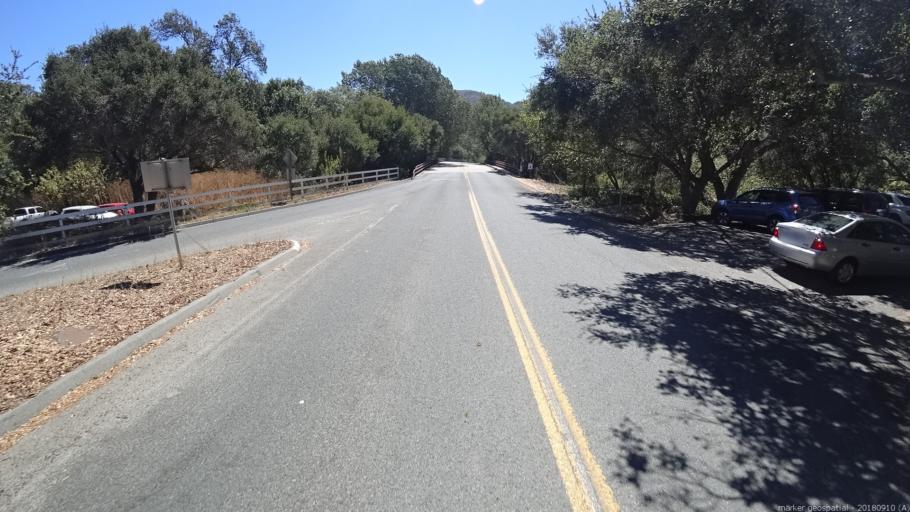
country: US
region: California
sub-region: Monterey County
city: Carmel Valley Village
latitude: 36.5216
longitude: -121.8061
